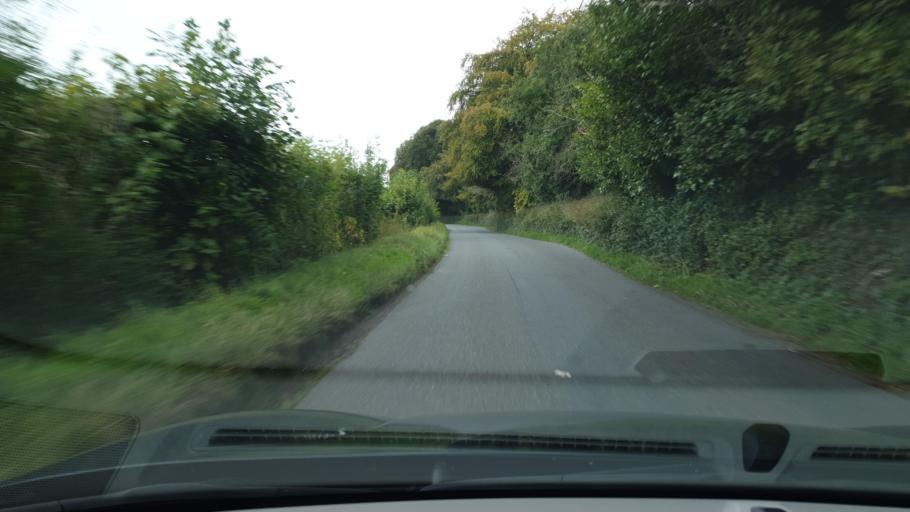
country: IE
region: Leinster
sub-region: Kildare
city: Kilcock
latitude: 53.3996
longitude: -6.6446
